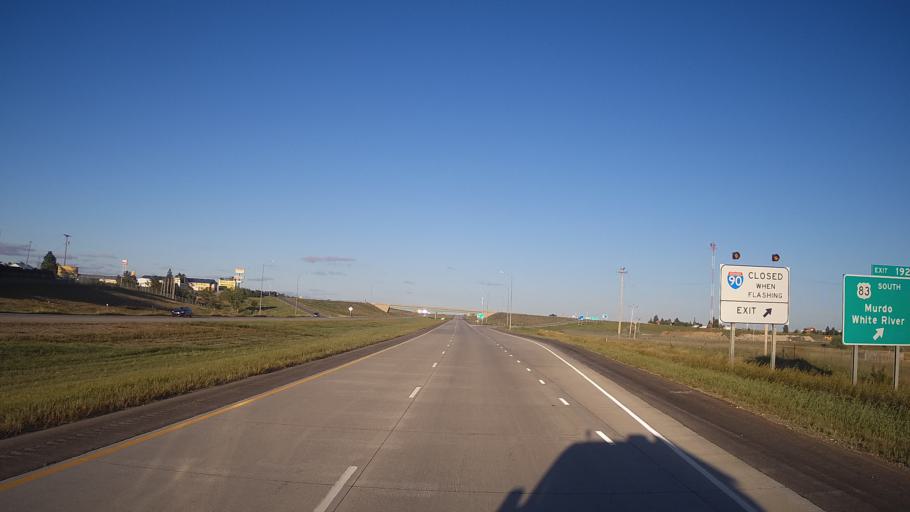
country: US
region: South Dakota
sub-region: Jones County
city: Murdo
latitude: 43.8830
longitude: -100.7131
